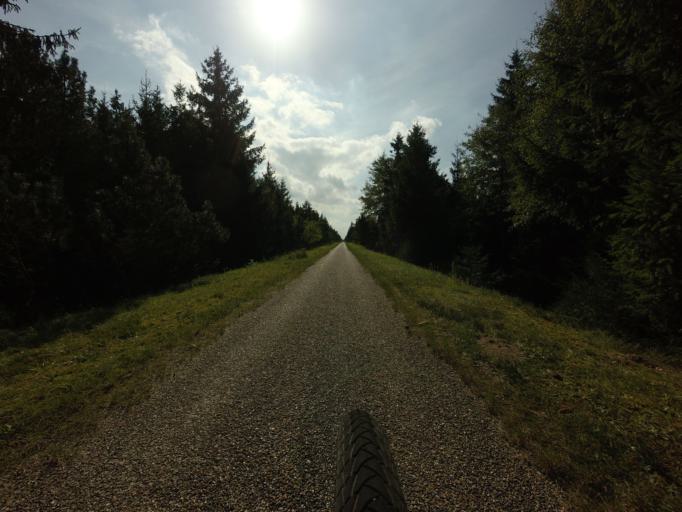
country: DK
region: Central Jutland
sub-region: Viborg Kommune
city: Karup
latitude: 56.2591
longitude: 9.1085
